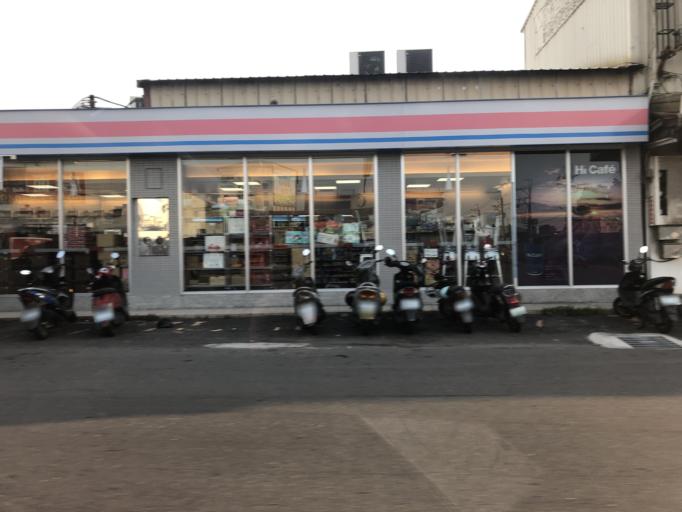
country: TW
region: Taiwan
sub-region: Tainan
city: Tainan
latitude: 23.0418
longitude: 120.2476
